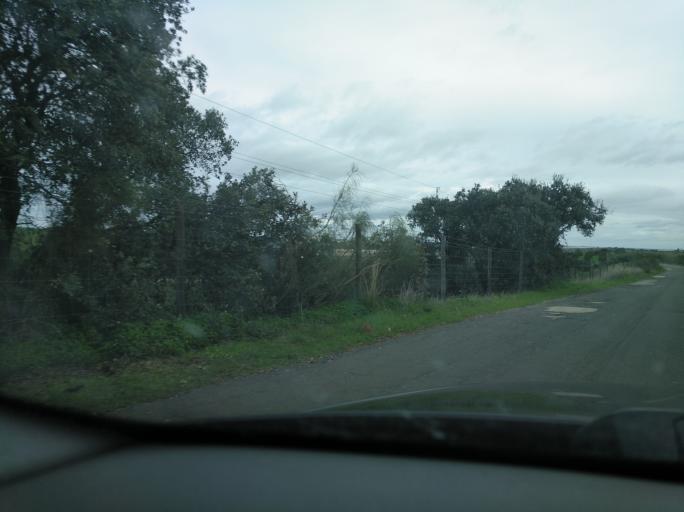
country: PT
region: Faro
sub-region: Vila Real de Santo Antonio
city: Monte Gordo
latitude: 37.1951
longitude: -7.5010
